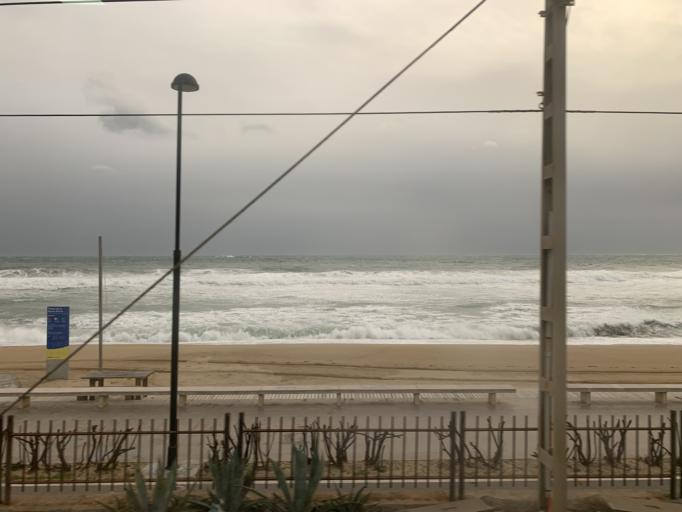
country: ES
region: Catalonia
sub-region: Provincia de Barcelona
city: Montgat
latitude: 41.4582
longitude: 2.2645
